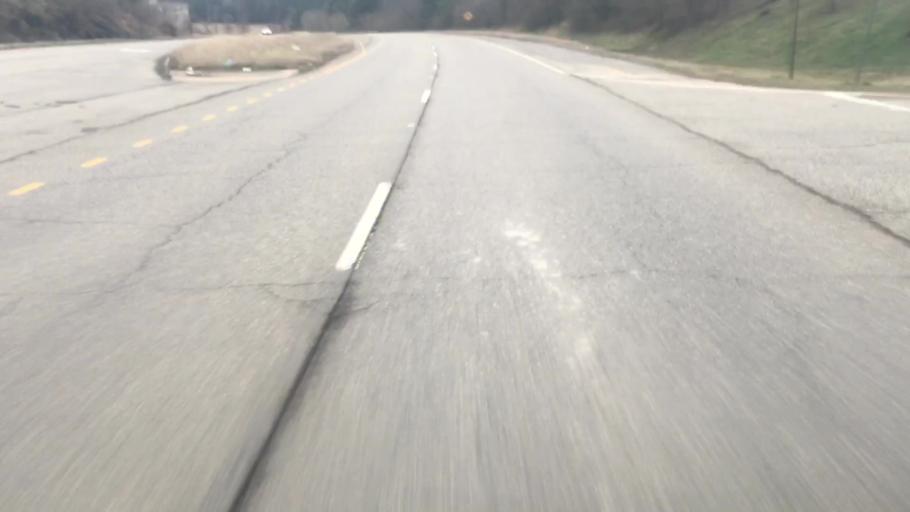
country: US
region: Alabama
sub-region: Walker County
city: Dora
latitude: 33.7951
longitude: -87.1080
